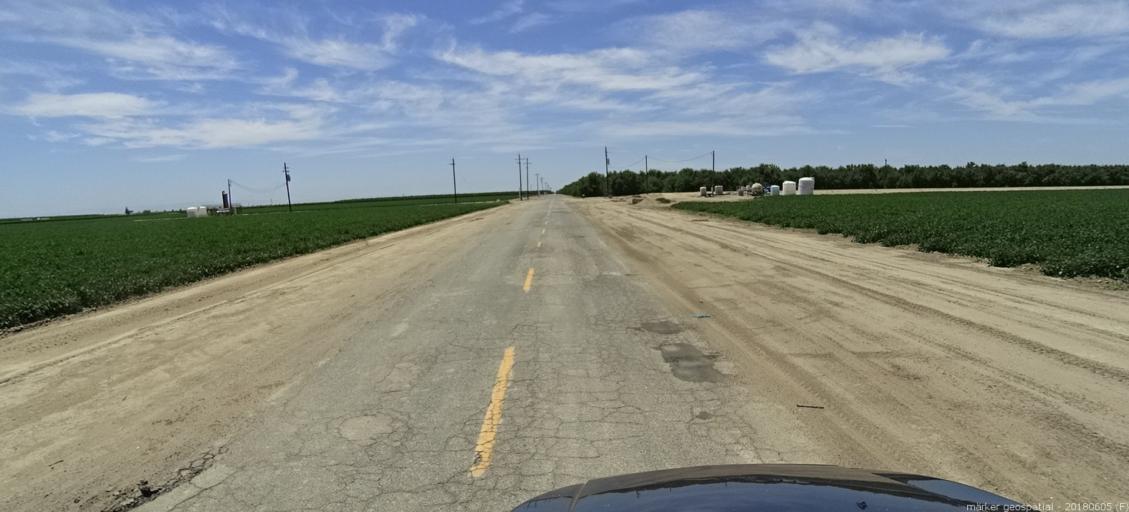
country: US
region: California
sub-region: Madera County
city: Chowchilla
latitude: 37.0906
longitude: -120.3900
